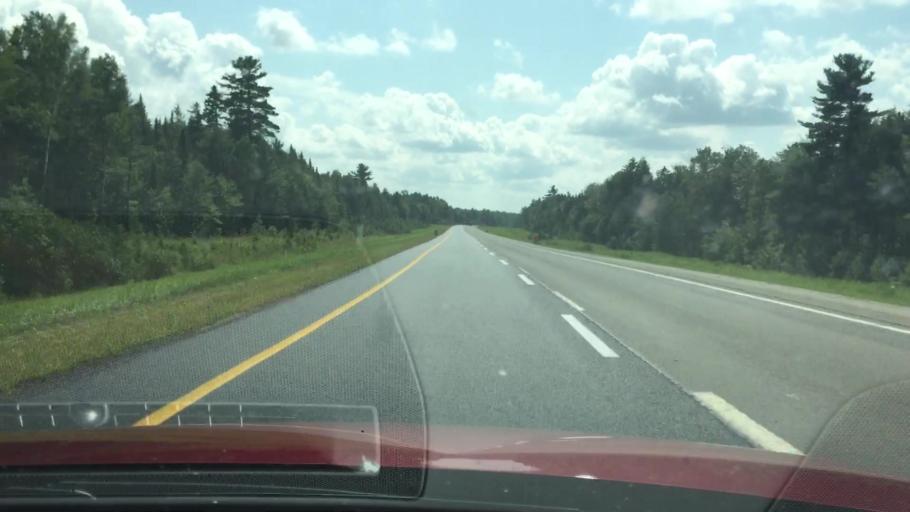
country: US
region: Maine
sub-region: Penobscot County
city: Medway
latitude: 45.6964
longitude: -68.4872
